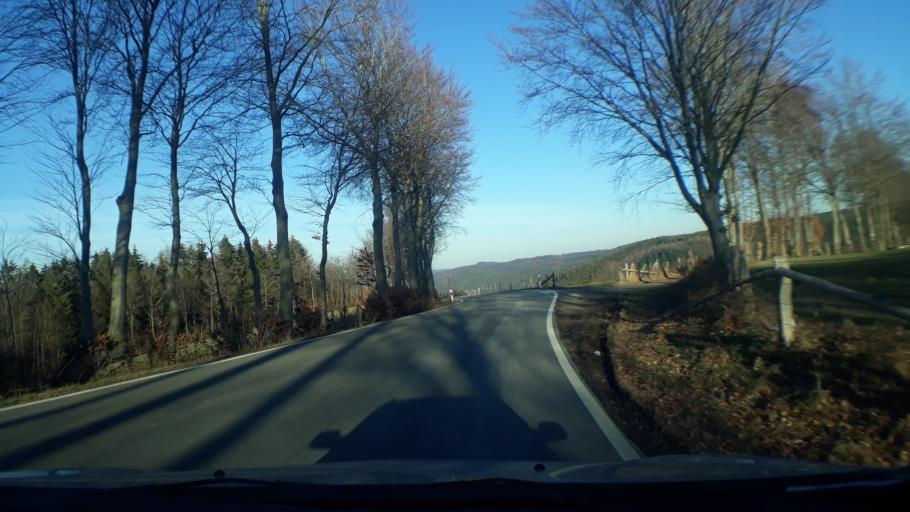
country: DE
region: North Rhine-Westphalia
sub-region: Regierungsbezirk Koln
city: Simmerath
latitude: 50.5557
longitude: 6.2987
